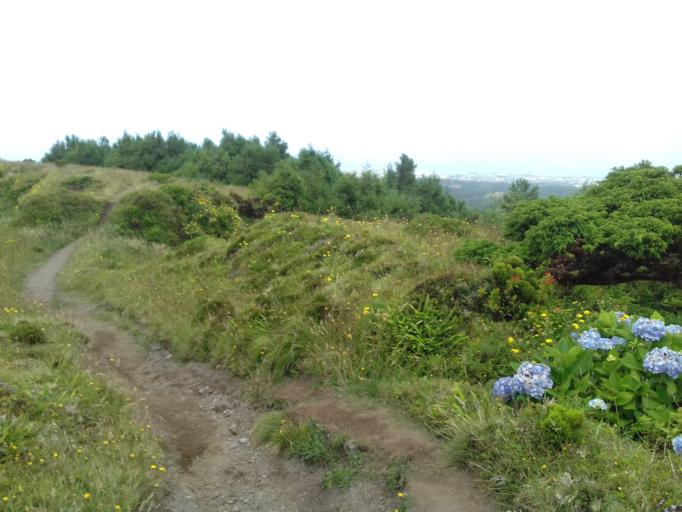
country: PT
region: Azores
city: Ribeira Grande
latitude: 38.5907
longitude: -28.7058
